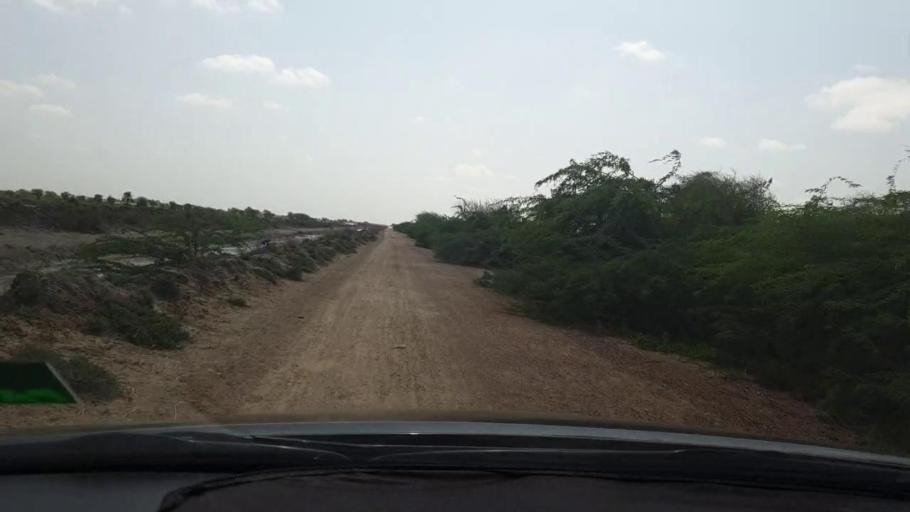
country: PK
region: Sindh
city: Tando Bago
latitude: 24.8285
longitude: 69.0617
